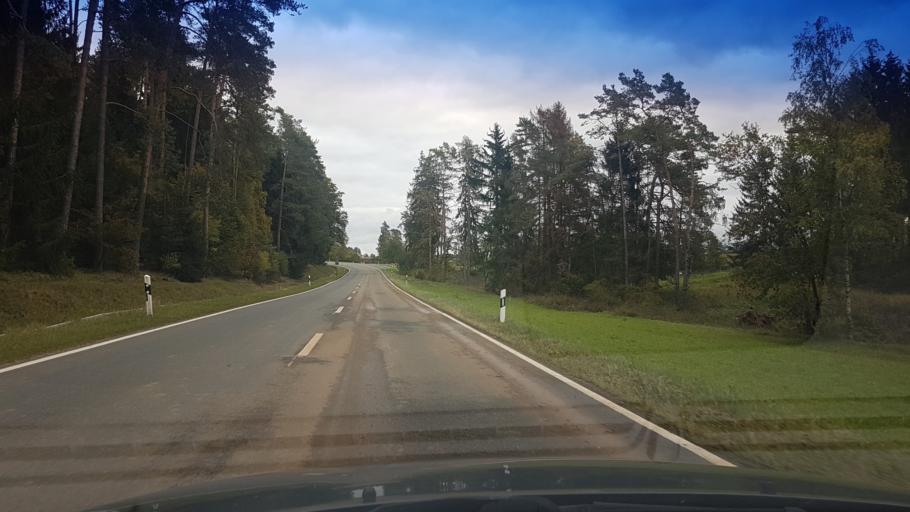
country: DE
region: Bavaria
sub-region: Upper Franconia
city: Stadelhofen
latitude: 50.0101
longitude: 11.2290
